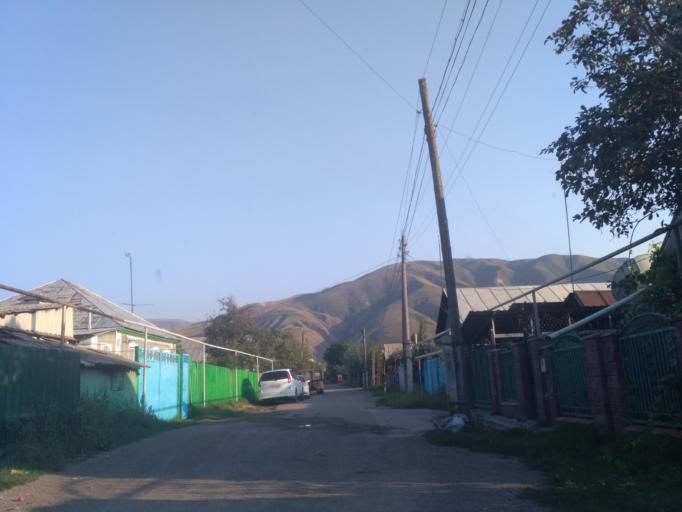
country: KZ
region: Almaty Oblysy
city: Burunday
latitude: 43.1641
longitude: 76.4048
